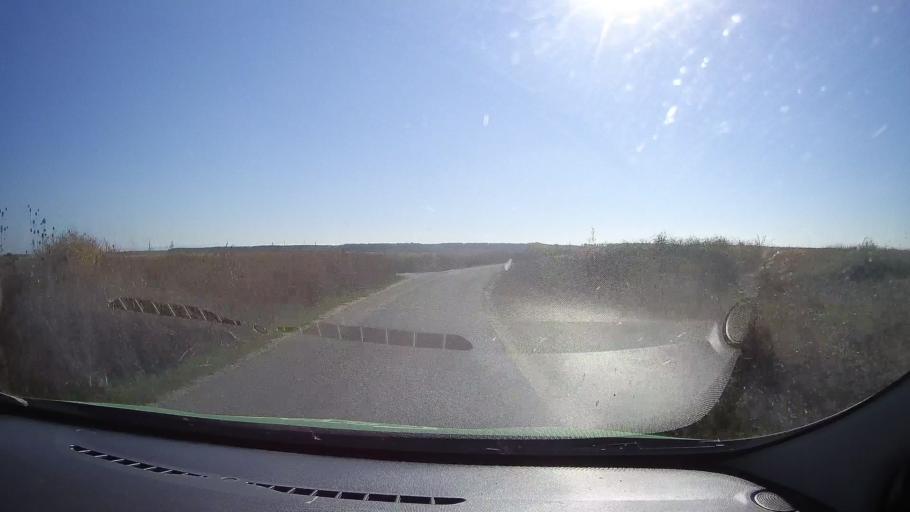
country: RO
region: Satu Mare
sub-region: Comuna Doba
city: Doba
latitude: 47.7318
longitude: 22.7240
